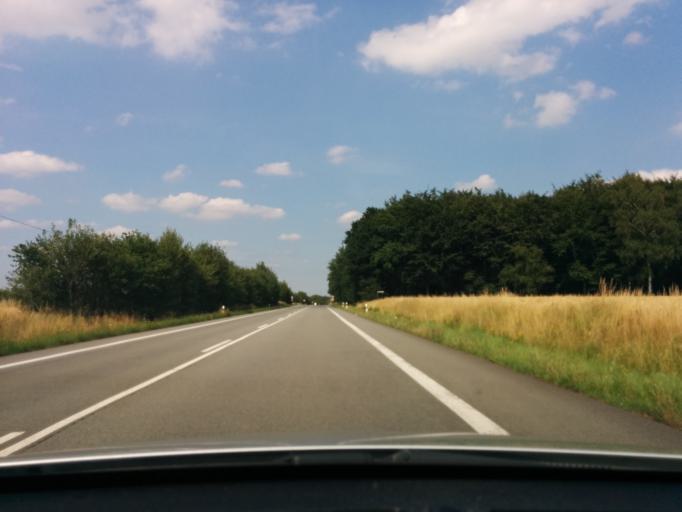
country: DE
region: North Rhine-Westphalia
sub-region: Regierungsbezirk Munster
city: Wettringen
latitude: 52.1920
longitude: 7.2902
